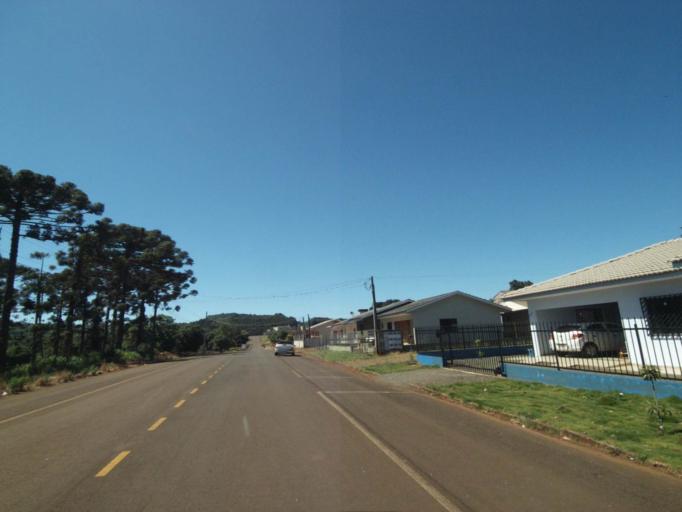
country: BR
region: Santa Catarina
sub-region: Sao Lourenco Do Oeste
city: Sao Lourenco dOeste
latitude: -26.2691
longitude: -52.7804
